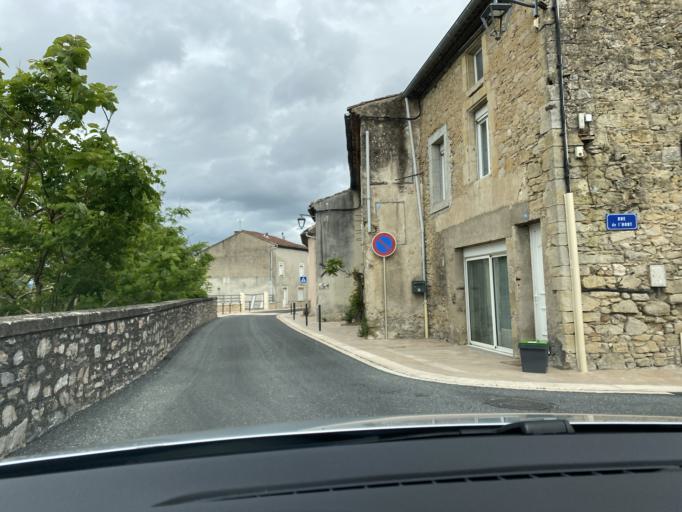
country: FR
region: Midi-Pyrenees
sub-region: Departement du Tarn
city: Saix
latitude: 43.5826
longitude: 2.1826
